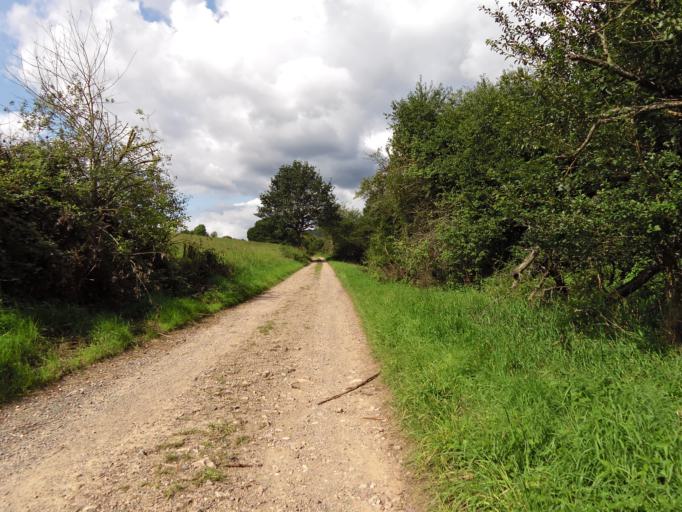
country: DE
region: Rheinland-Pfalz
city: Steinbach am Donnersberg
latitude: 49.5976
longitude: 7.9418
